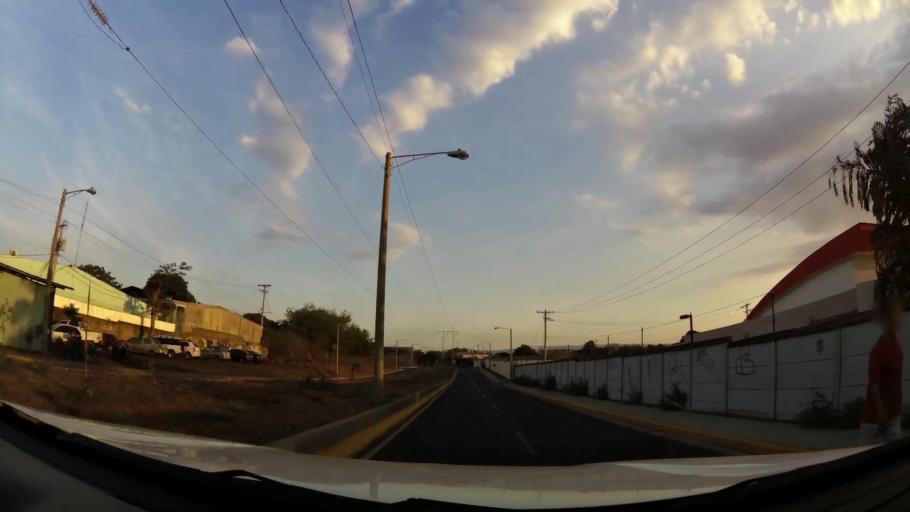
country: NI
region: Managua
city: Managua
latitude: 12.1508
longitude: -86.2344
